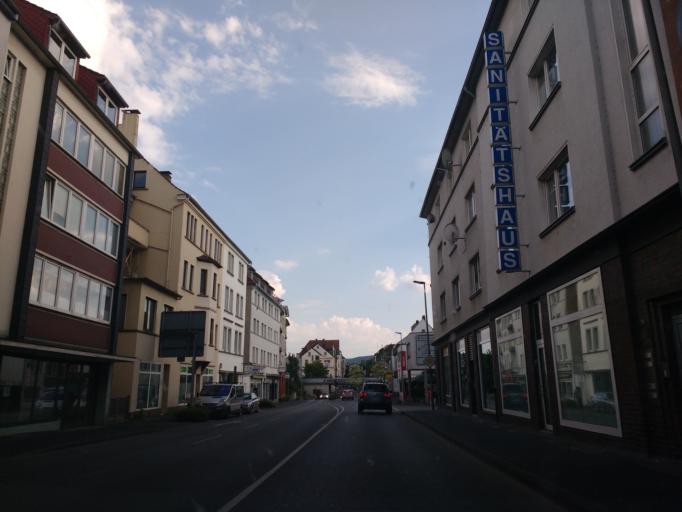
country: DE
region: North Rhine-Westphalia
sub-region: Regierungsbezirk Detmold
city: Detmold
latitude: 51.9416
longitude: 8.8764
